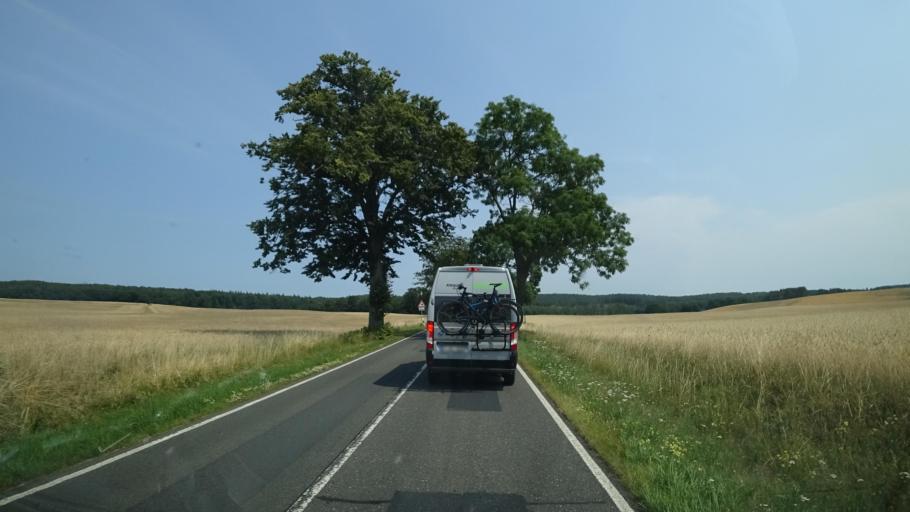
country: DE
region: Mecklenburg-Vorpommern
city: Seebad Heringsdorf
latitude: 53.8921
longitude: 14.1526
